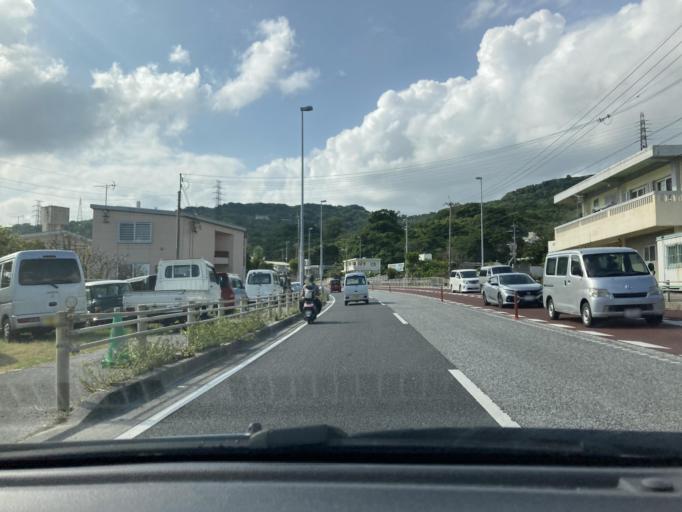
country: JP
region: Okinawa
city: Ginowan
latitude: 26.2776
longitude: 127.8059
